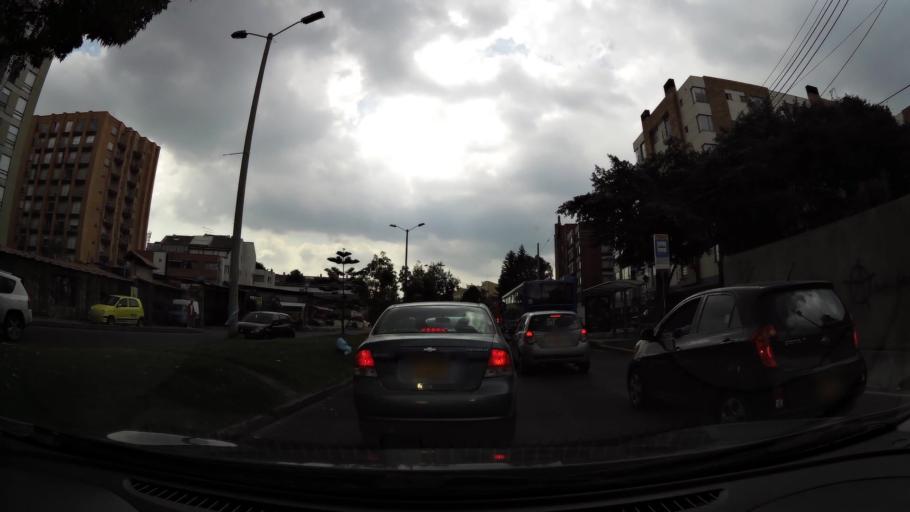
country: CO
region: Bogota D.C.
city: Barrio San Luis
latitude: 4.7289
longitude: -74.0399
